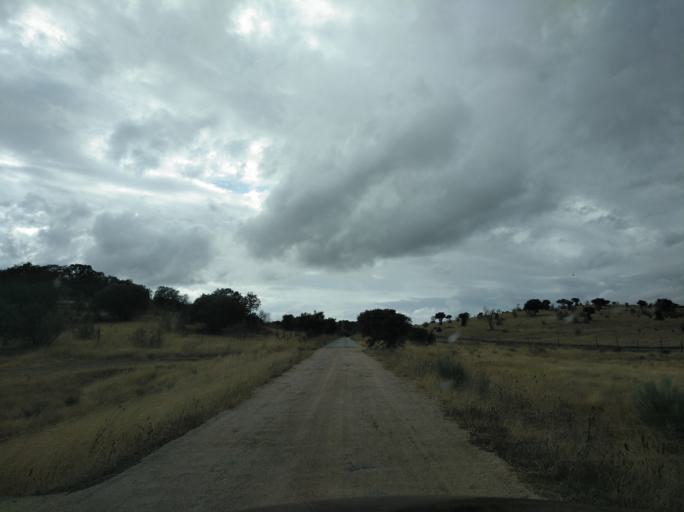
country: PT
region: Portalegre
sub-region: Campo Maior
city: Campo Maior
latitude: 39.0361
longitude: -7.1363
